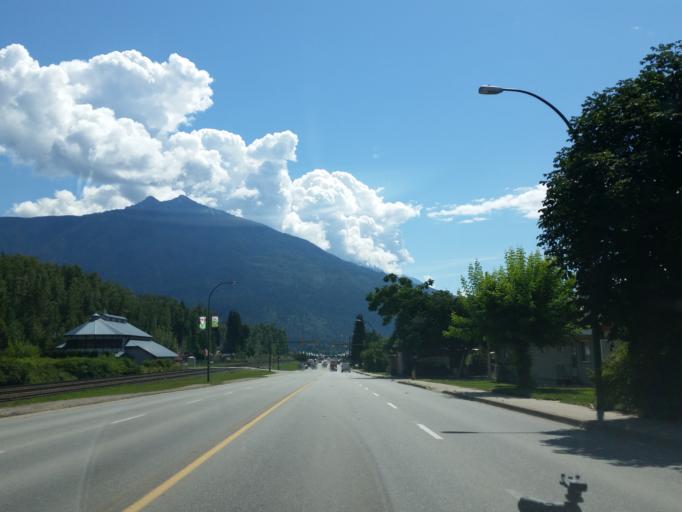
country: CA
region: British Columbia
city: Revelstoke
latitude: 51.0049
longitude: -118.2035
